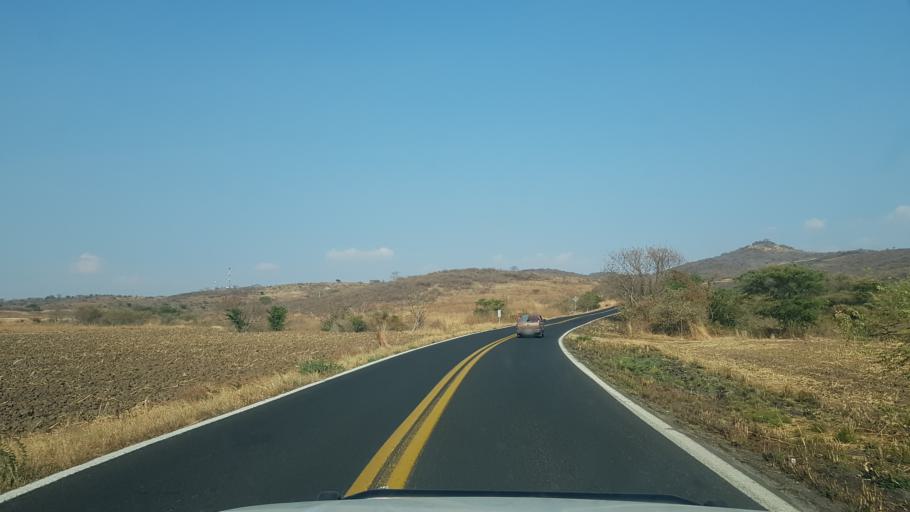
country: MX
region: Puebla
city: Calmeca
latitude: 18.6419
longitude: -98.6158
